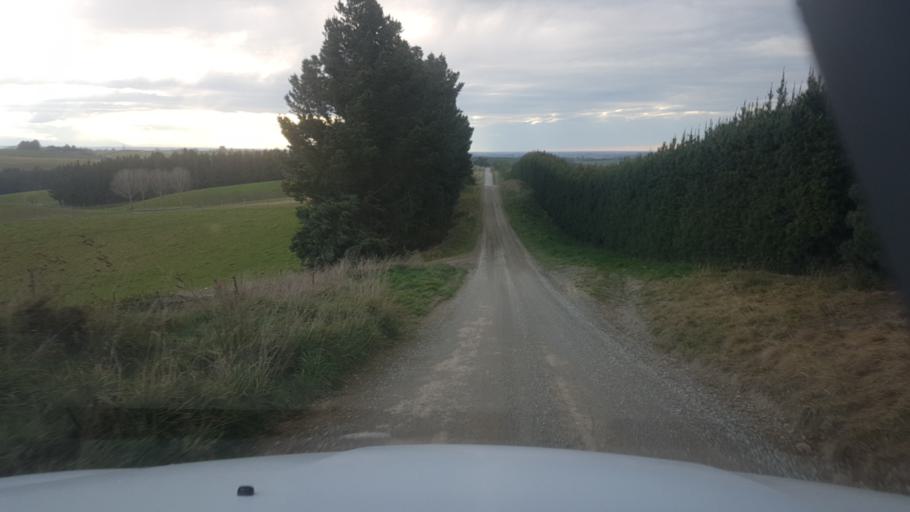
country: NZ
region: Canterbury
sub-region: Timaru District
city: Pleasant Point
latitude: -44.3437
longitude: 171.1389
